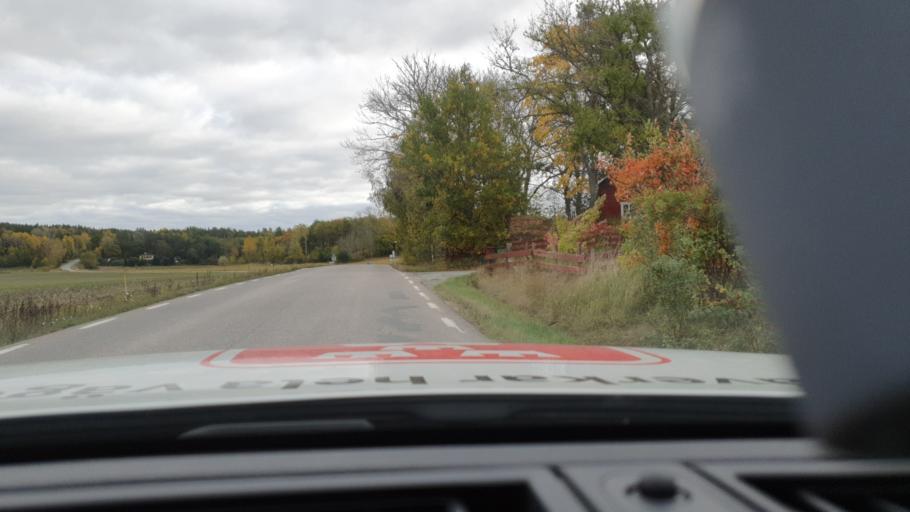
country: SE
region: Stockholm
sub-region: Upplands-Bro Kommun
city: Bro
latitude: 59.5073
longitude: 17.5810
